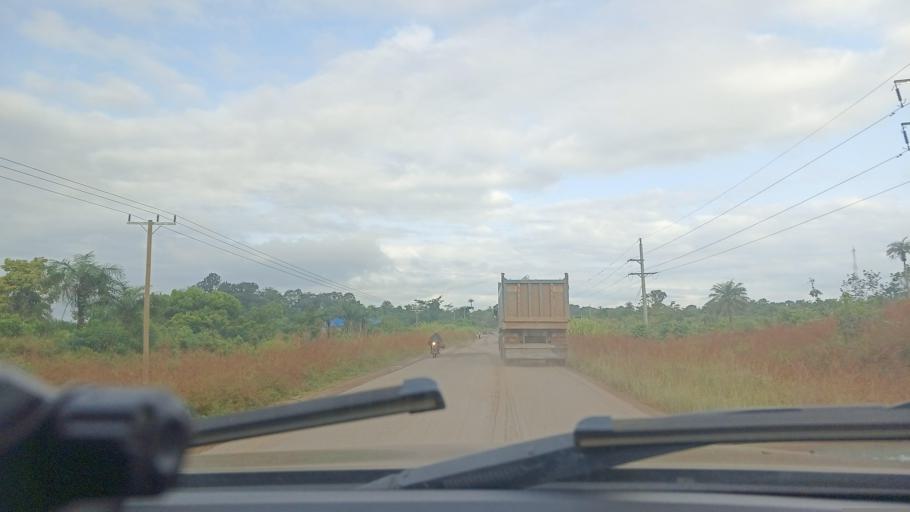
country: LR
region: Montserrado
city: Monrovia
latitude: 6.5781
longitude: -10.8870
